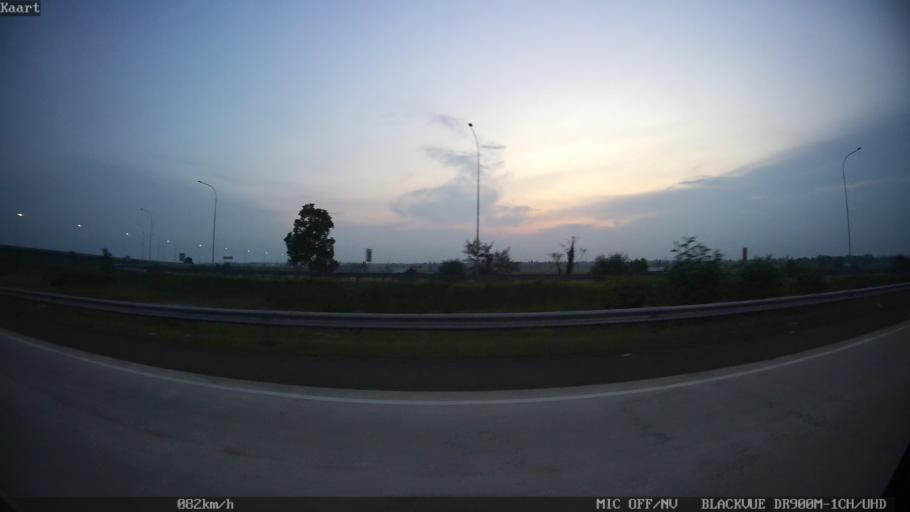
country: ID
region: Lampung
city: Sidorejo
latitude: -5.6061
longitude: 105.5559
